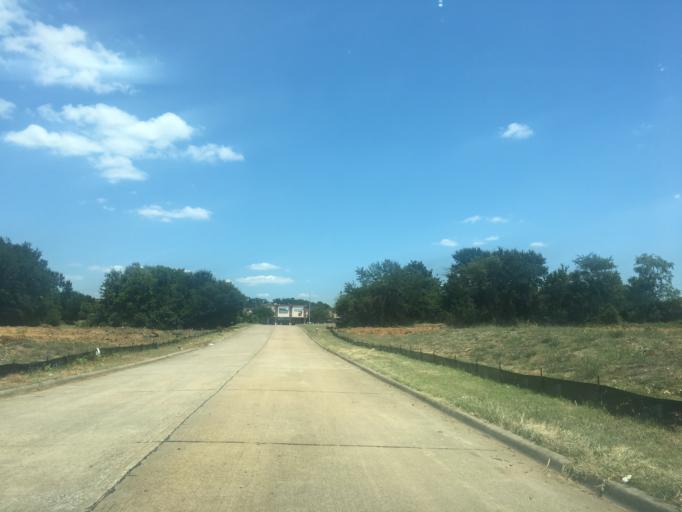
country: US
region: Texas
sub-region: Denton County
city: Lewisville
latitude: 33.0217
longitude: -96.9949
